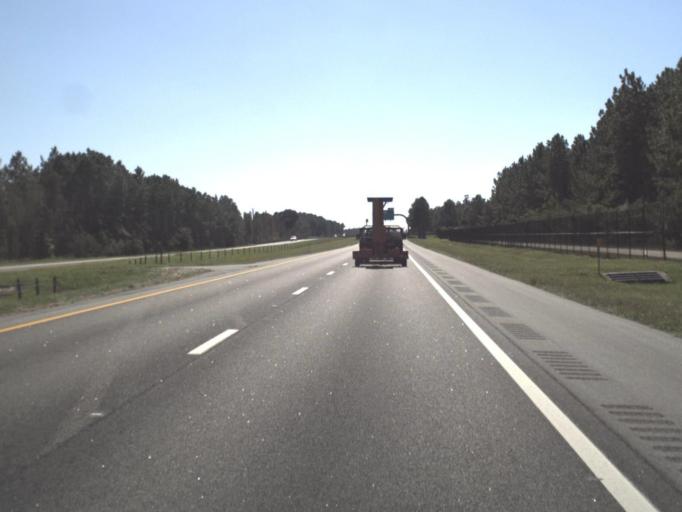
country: US
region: Florida
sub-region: Pasco County
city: Odessa
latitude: 28.2185
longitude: -82.5495
